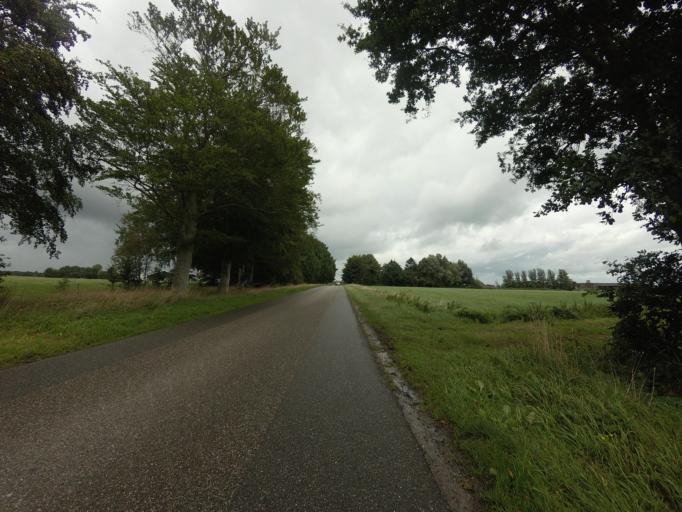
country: NL
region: Drenthe
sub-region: Gemeente Westerveld
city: Dwingeloo
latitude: 52.9723
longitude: 6.2917
